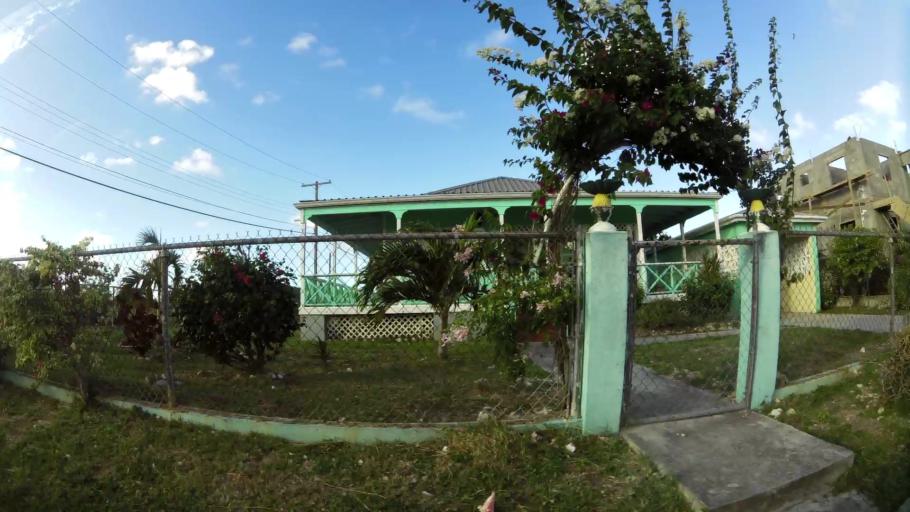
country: AG
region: Saint George
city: Piggotts
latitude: 17.1125
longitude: -61.7937
